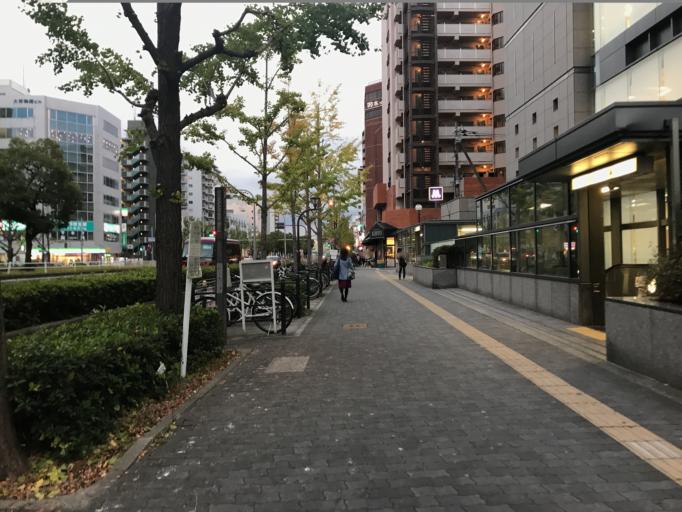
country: JP
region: Osaka
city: Osaka-shi
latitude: 34.6738
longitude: 135.4868
